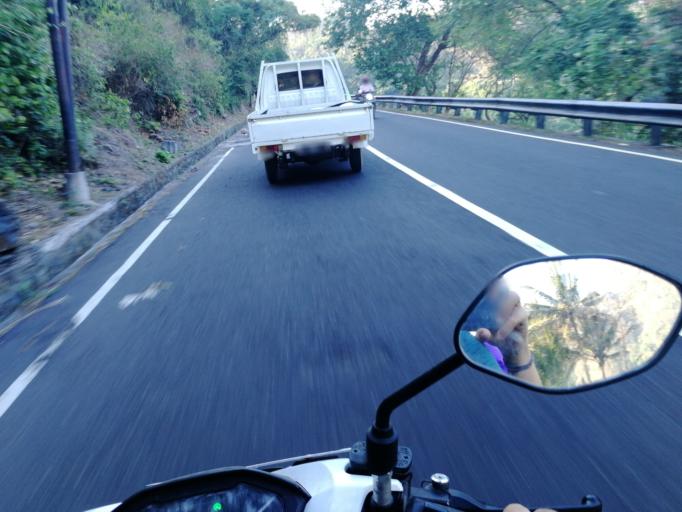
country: ID
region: Bali
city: Tistagede
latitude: -8.3684
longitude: 115.6090
